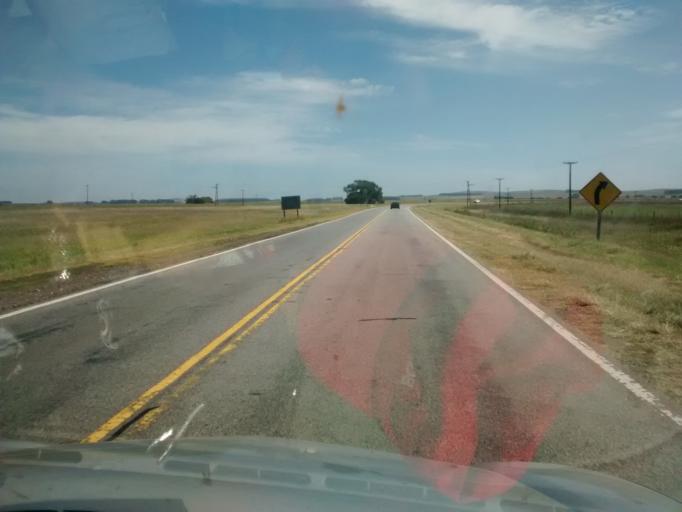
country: AR
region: Buenos Aires
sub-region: Partido de Balcarce
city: Balcarce
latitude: -37.6690
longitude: -58.5401
